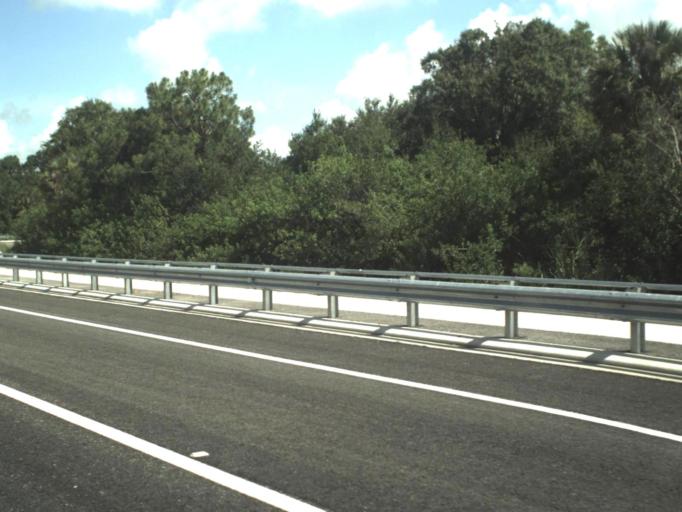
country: US
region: Florida
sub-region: Martin County
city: Indiantown
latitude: 27.0153
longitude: -80.4588
